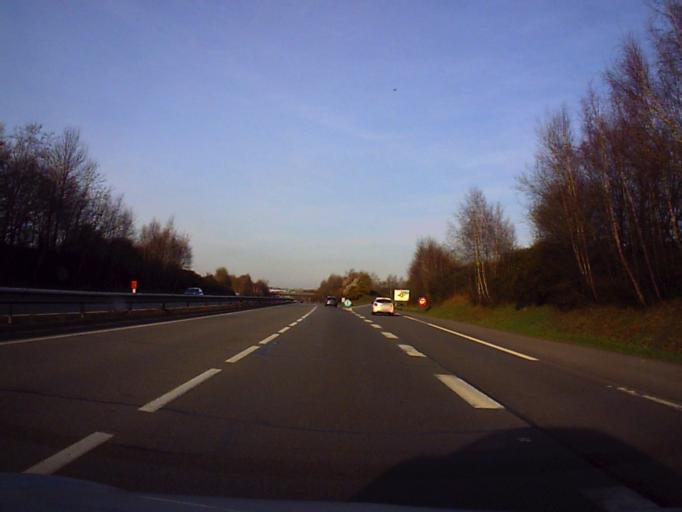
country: FR
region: Brittany
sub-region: Departement d'Ille-et-Vilaine
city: Chavagne
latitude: 48.0766
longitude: -1.7975
